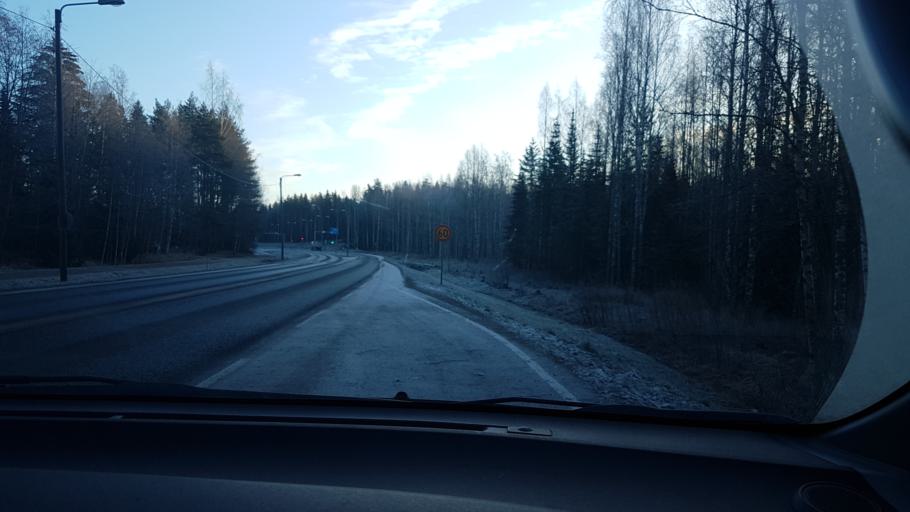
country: FI
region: Uusimaa
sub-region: Helsinki
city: Tuusula
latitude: 60.3953
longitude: 25.0588
